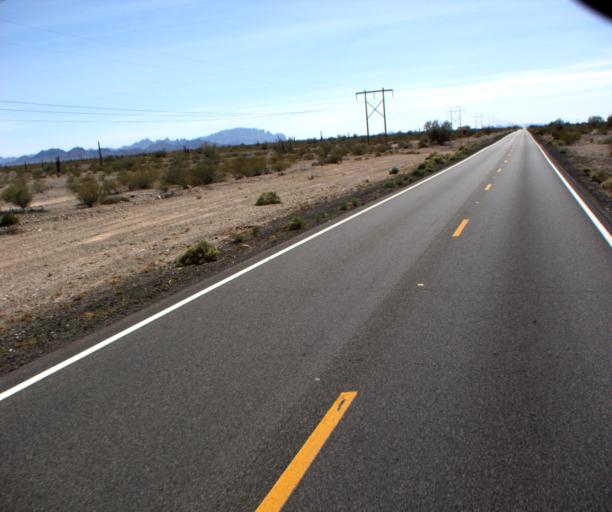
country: US
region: Arizona
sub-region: La Paz County
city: Quartzsite
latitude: 33.5939
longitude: -114.2171
